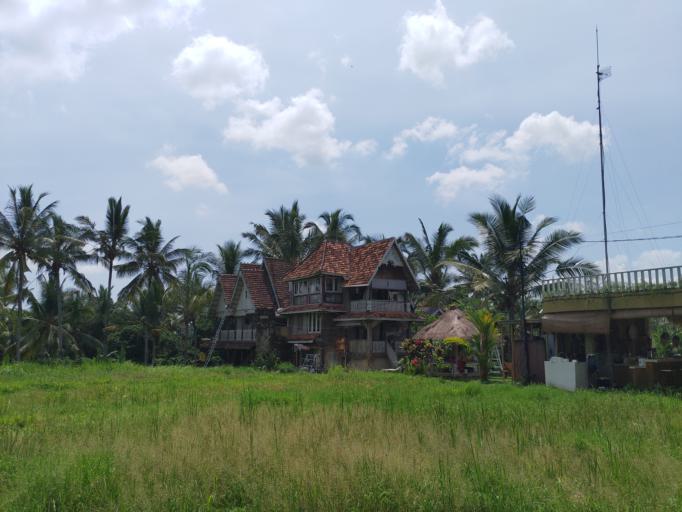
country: ID
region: Bali
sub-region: Kabupaten Gianyar
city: Ubud
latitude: -8.4938
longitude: 115.2599
